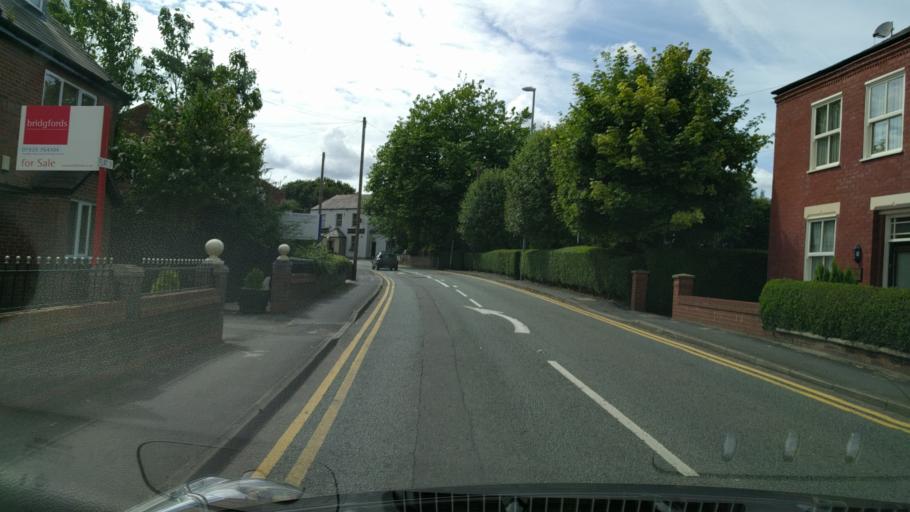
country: GB
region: England
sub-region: Warrington
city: Culcheth
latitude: 53.4519
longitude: -2.5200
